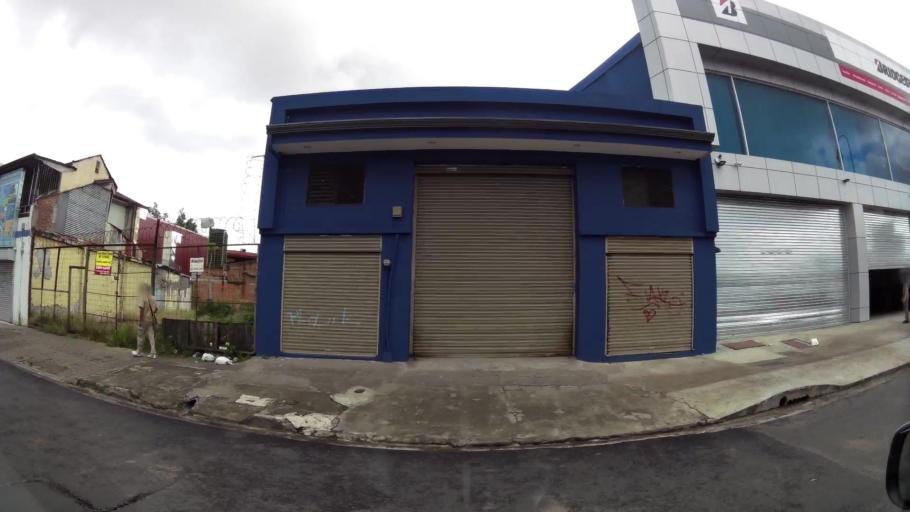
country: CR
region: San Jose
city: San Jose
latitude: 9.9263
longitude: -84.0748
